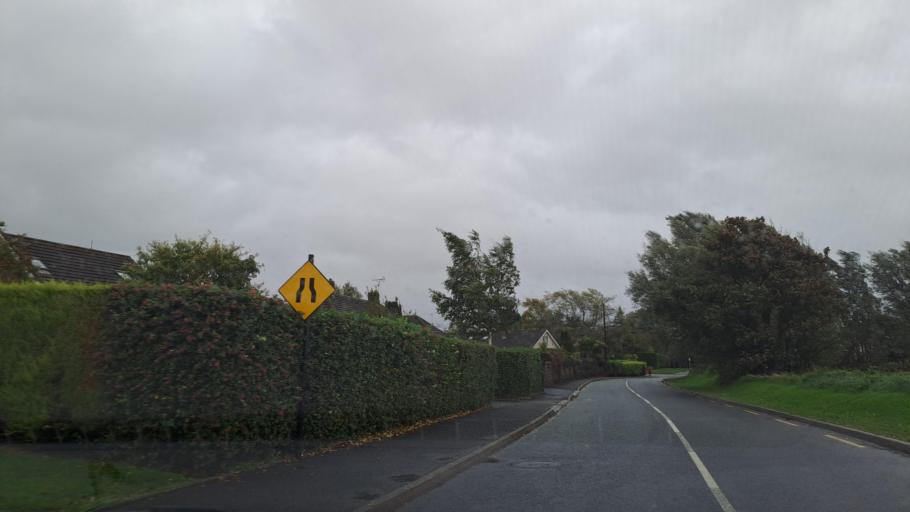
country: IE
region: Leinster
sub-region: Lu
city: Blackrock
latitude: 53.9575
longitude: -6.3735
